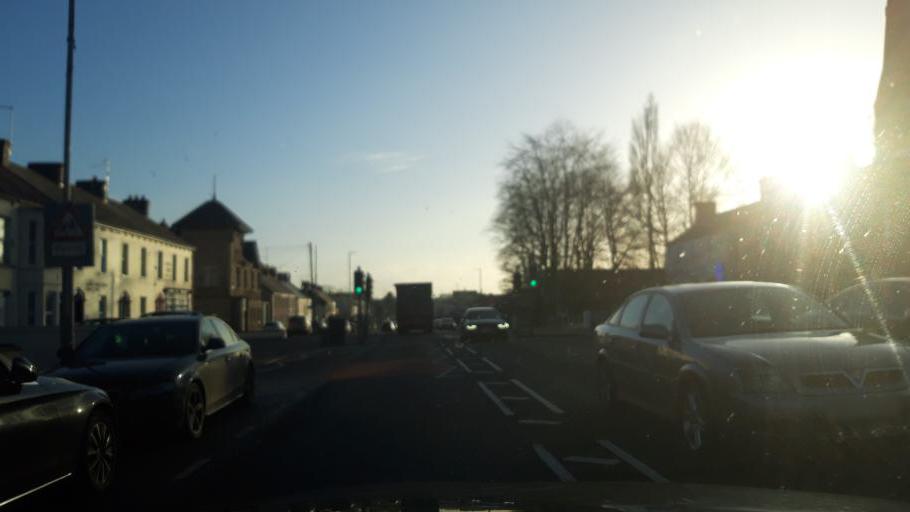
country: GB
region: Northern Ireland
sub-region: Cookstown District
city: Cookstown
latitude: 54.6431
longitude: -6.7446
